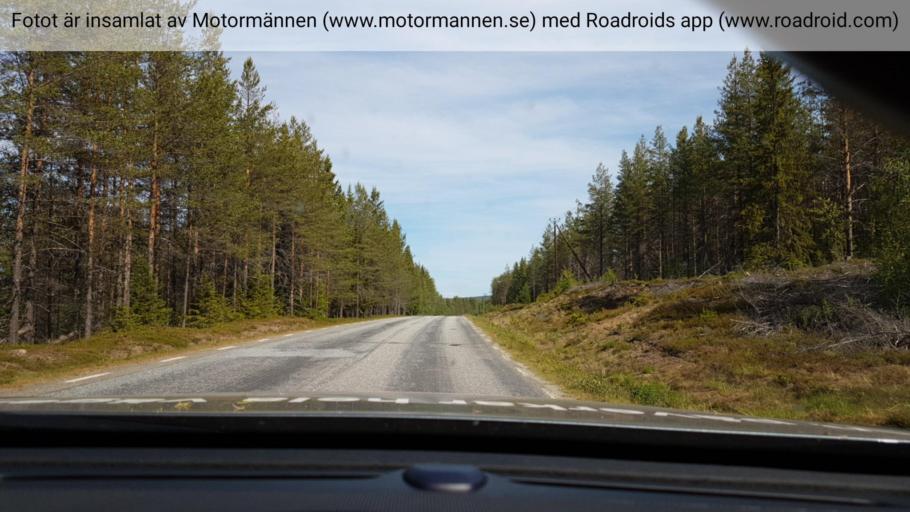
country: SE
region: Vaesterbotten
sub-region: Vilhelmina Kommun
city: Sjoberg
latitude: 64.4768
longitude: 15.9455
